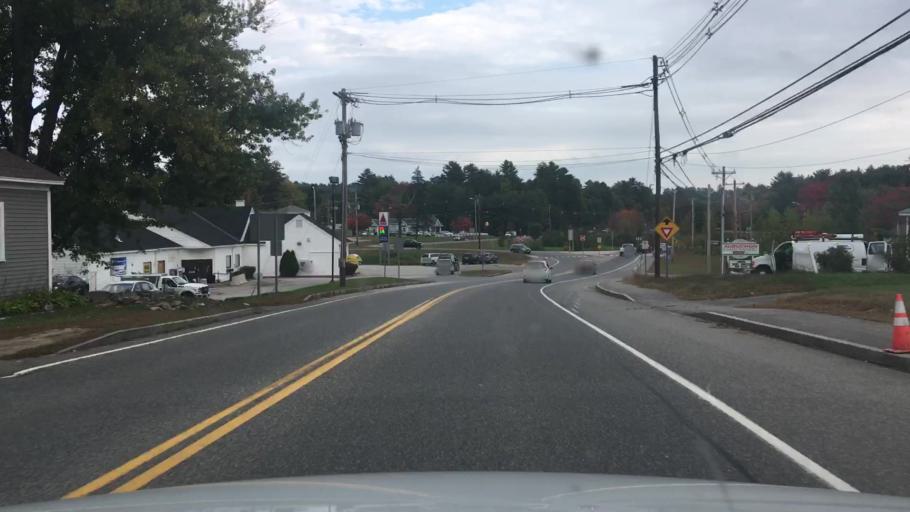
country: US
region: New Hampshire
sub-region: Strafford County
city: New Durham
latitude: 43.4523
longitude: -71.2141
